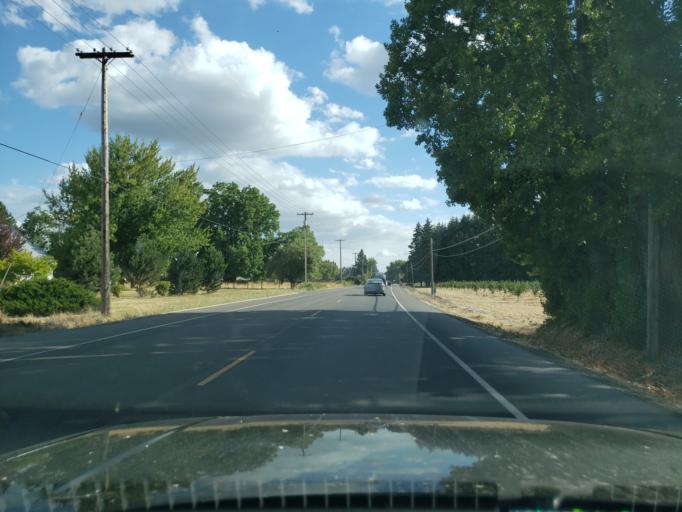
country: US
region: Oregon
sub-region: Yamhill County
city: McMinnville
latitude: 45.1798
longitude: -123.2099
